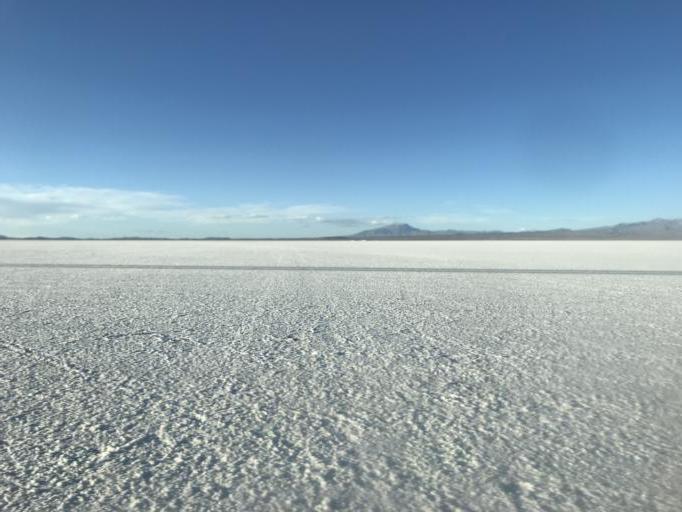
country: BO
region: Potosi
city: Colchani
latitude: -20.3640
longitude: -67.0115
